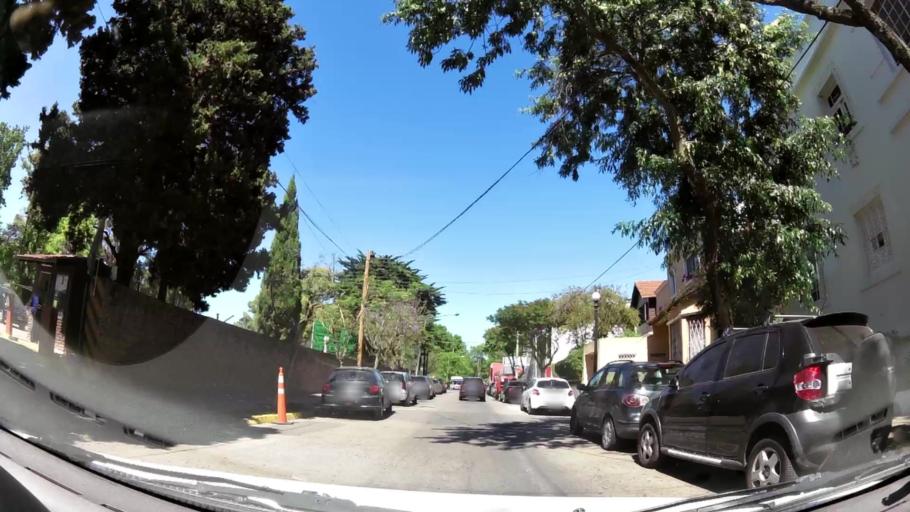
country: AR
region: Buenos Aires
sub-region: Partido de Vicente Lopez
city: Olivos
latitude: -34.5108
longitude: -58.4776
